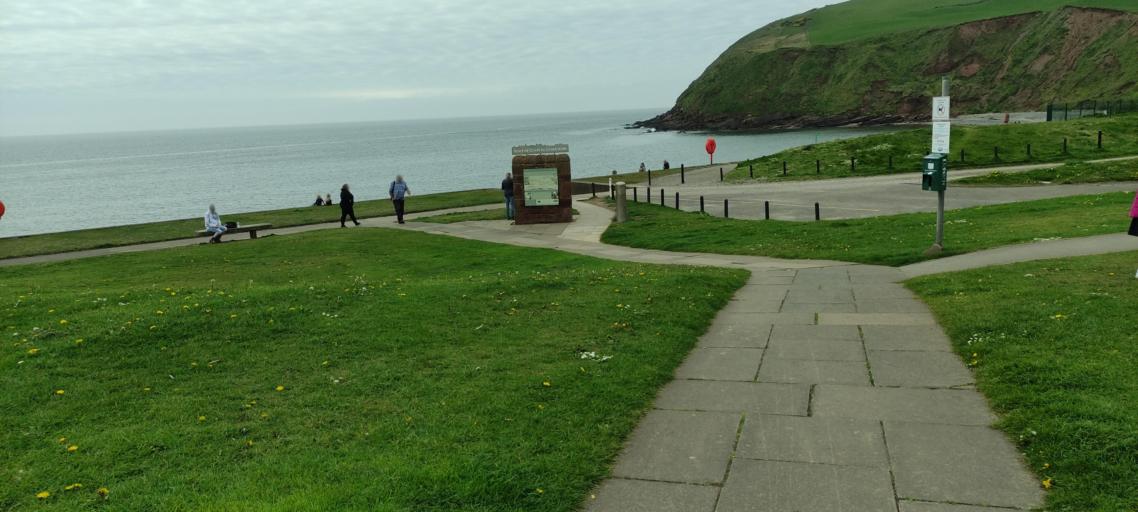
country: GB
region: England
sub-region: Cumbria
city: Saint Bees
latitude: 54.4909
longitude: -3.6059
